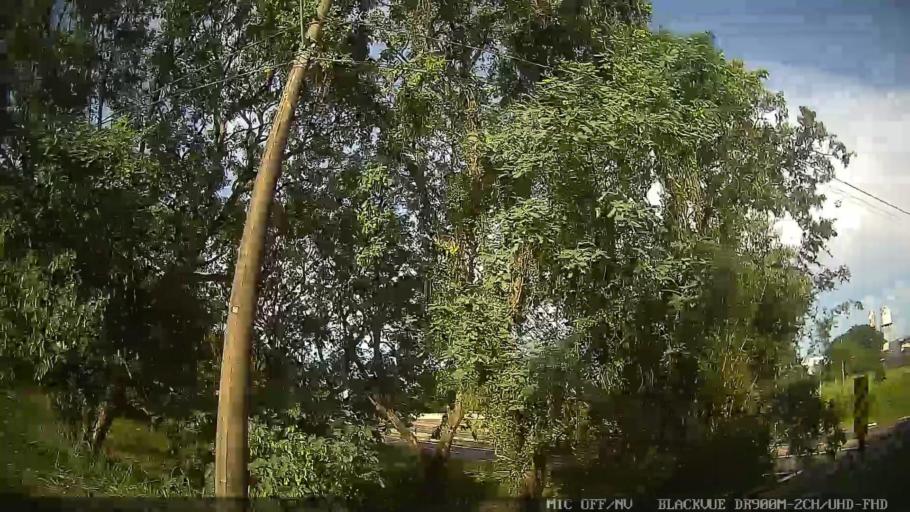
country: BR
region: Sao Paulo
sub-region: Tiete
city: Tiete
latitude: -23.0861
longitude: -47.7194
